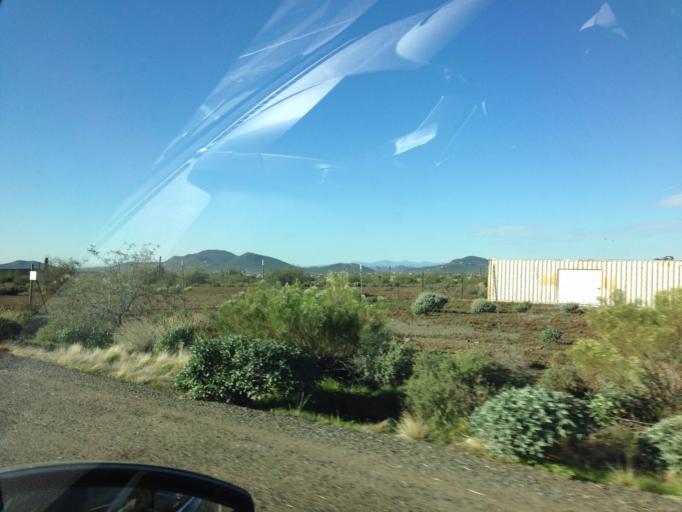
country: US
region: Arizona
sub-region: Maricopa County
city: Anthem
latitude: 33.8484
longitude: -112.0628
